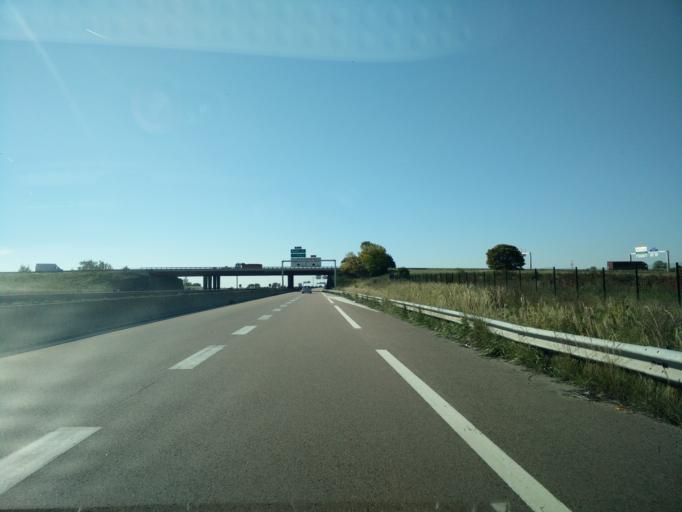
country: FR
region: Ile-de-France
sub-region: Departement de Seine-et-Marne
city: Mitry-Mory
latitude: 49.0014
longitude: 2.6385
